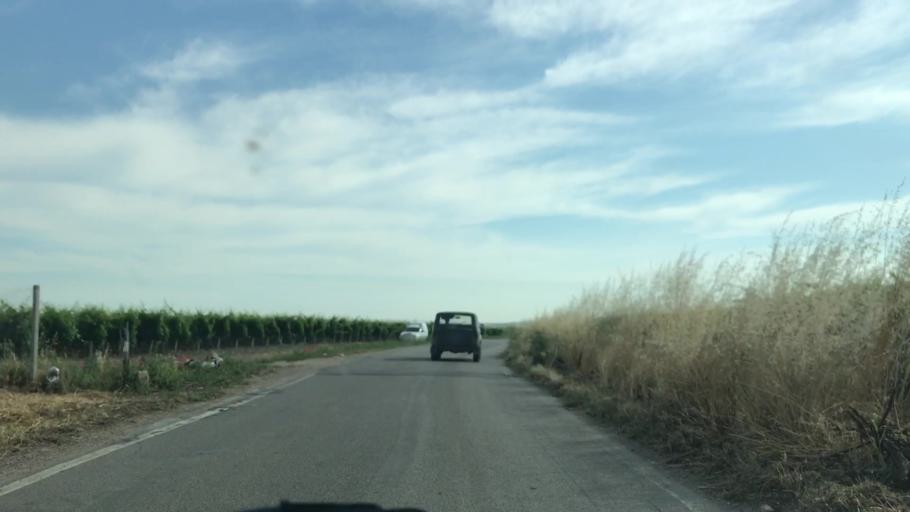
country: IT
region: Apulia
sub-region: Provincia di Taranto
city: San Giorgio Ionico
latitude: 40.4349
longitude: 17.3467
